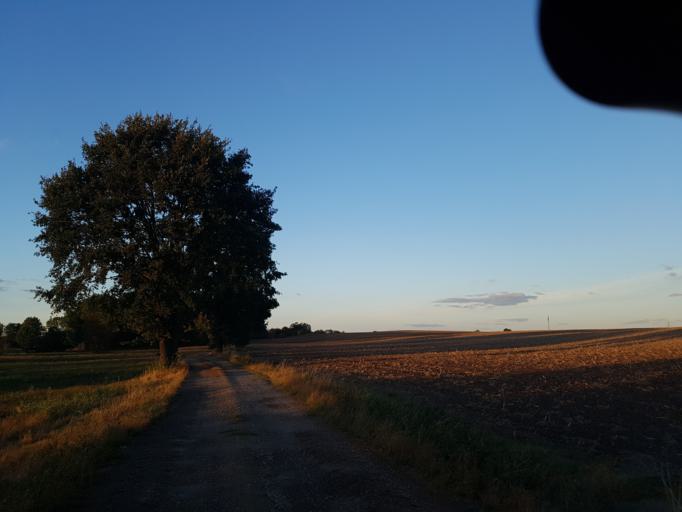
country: DE
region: Saxony
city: Oschatz
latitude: 51.2879
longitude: 13.1563
